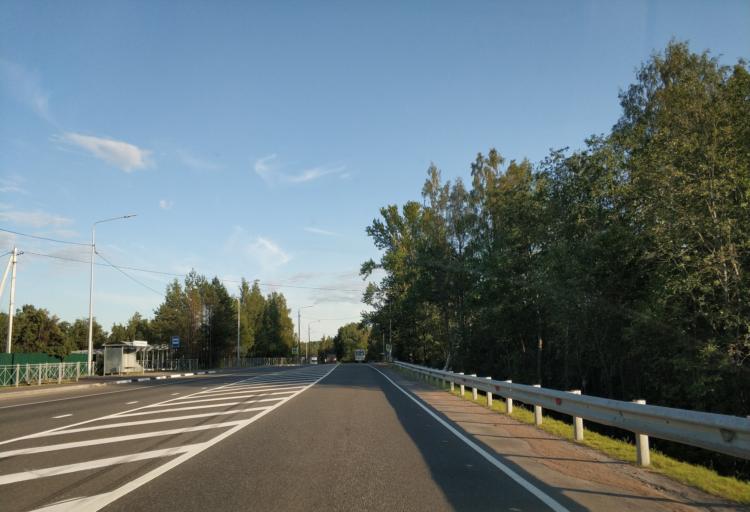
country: RU
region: Leningrad
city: Sapernoye
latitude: 60.7047
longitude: 29.9690
